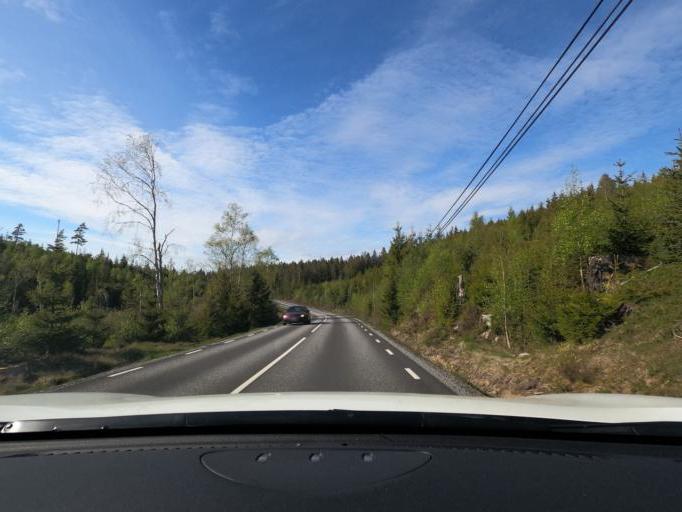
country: SE
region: Vaestra Goetaland
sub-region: Harryda Kommun
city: Landvetter
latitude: 57.6322
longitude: 12.2655
